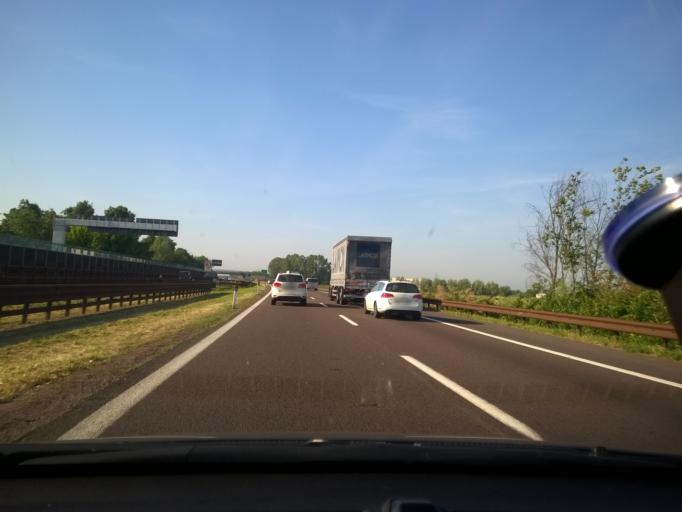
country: IT
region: Emilia-Romagna
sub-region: Provincia di Modena
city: Santa Croce Scuole
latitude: 44.7613
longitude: 10.8437
